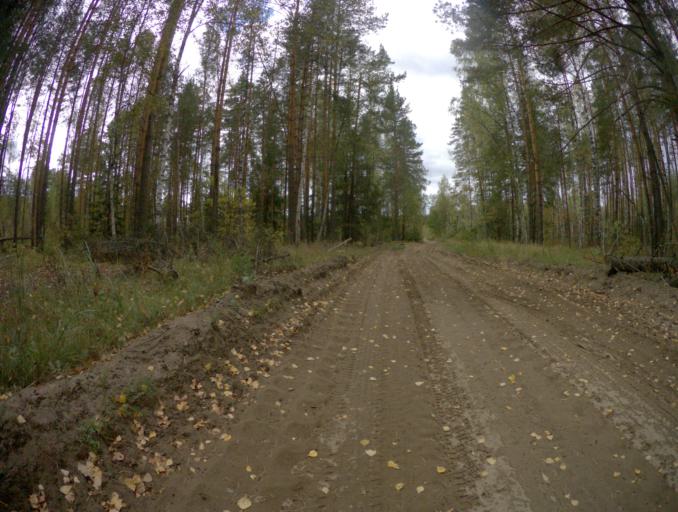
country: RU
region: Vladimir
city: Petushki
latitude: 55.8636
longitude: 39.5375
